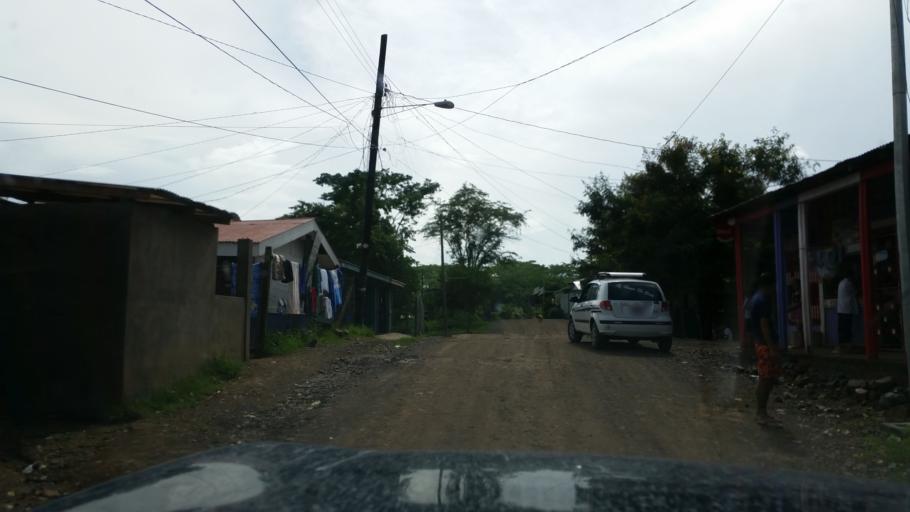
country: NI
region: Atlantico Norte (RAAN)
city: Siuna
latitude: 13.7160
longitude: -84.7706
